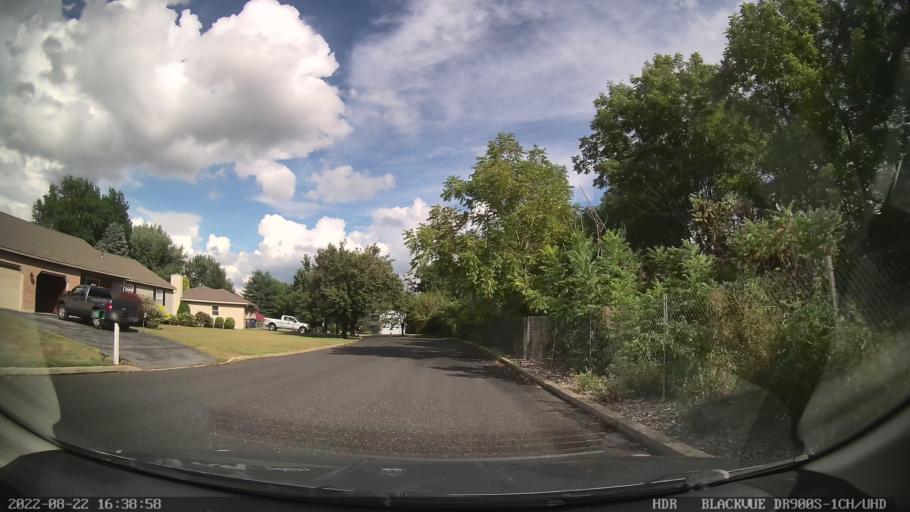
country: US
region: Pennsylvania
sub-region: Lehigh County
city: Dorneyville
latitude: 40.5704
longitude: -75.5330
